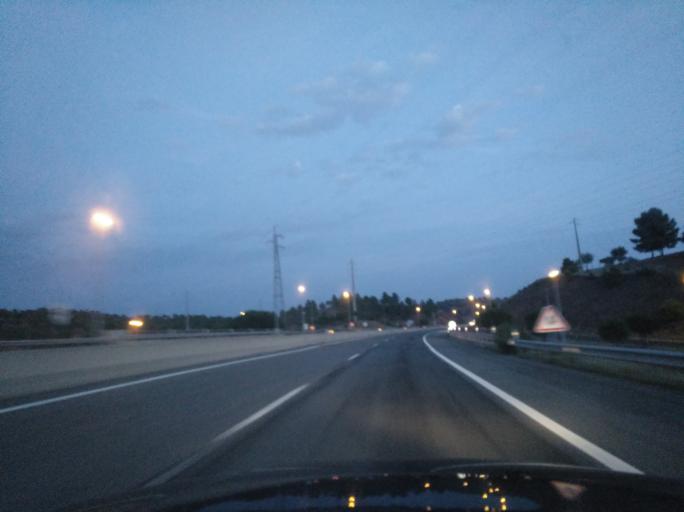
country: PT
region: Faro
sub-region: Portimao
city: Portimao
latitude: 37.1781
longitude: -8.5299
